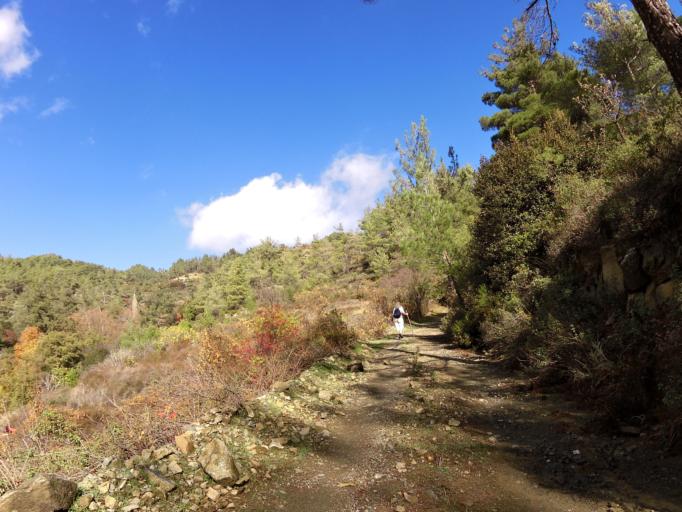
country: CY
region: Limassol
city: Kyperounta
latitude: 34.9272
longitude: 32.9455
